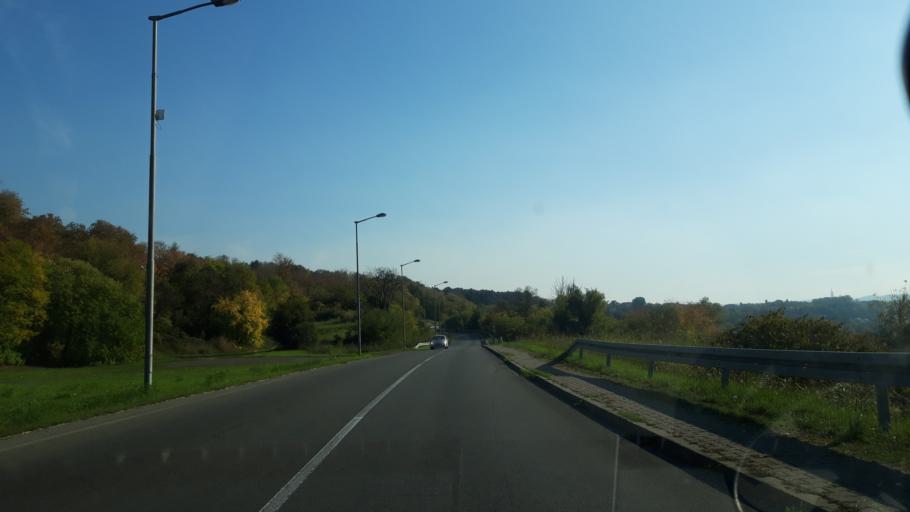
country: RS
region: Autonomna Pokrajina Vojvodina
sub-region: Juznobacki Okrug
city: Petrovaradin
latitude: 45.2482
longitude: 19.8652
